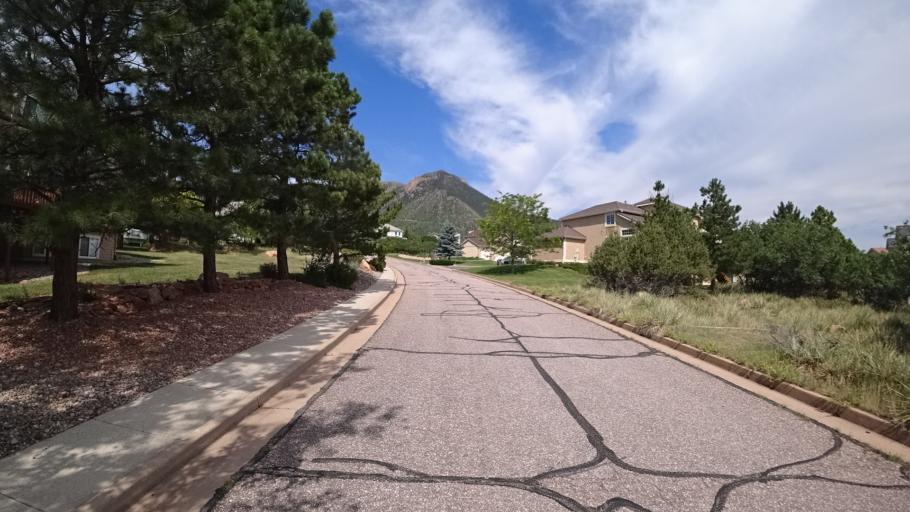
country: US
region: Colorado
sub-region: El Paso County
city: Air Force Academy
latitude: 38.9529
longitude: -104.8781
